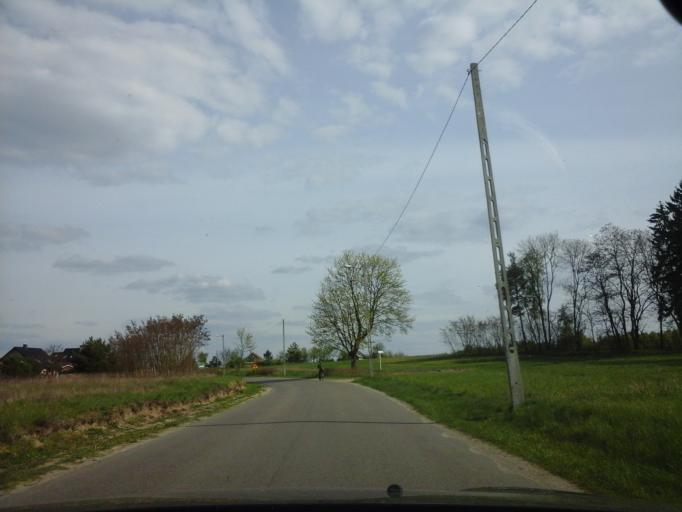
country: PL
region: West Pomeranian Voivodeship
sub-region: Powiat choszczenski
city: Bierzwnik
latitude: 53.0405
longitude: 15.6475
